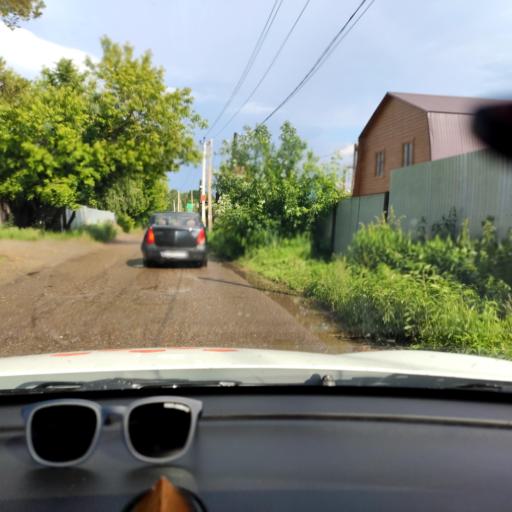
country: RU
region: Tatarstan
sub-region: Zelenodol'skiy Rayon
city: Vasil'yevo
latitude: 55.8276
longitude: 48.7574
